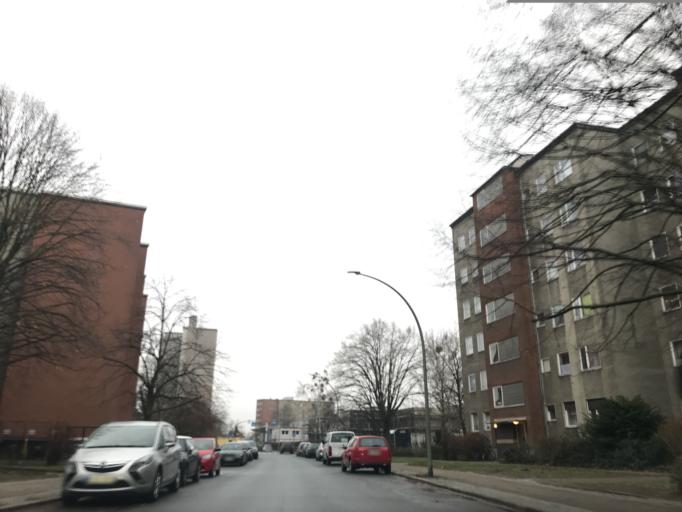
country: DE
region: Berlin
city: Falkenhagener Feld
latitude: 52.5526
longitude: 13.1790
